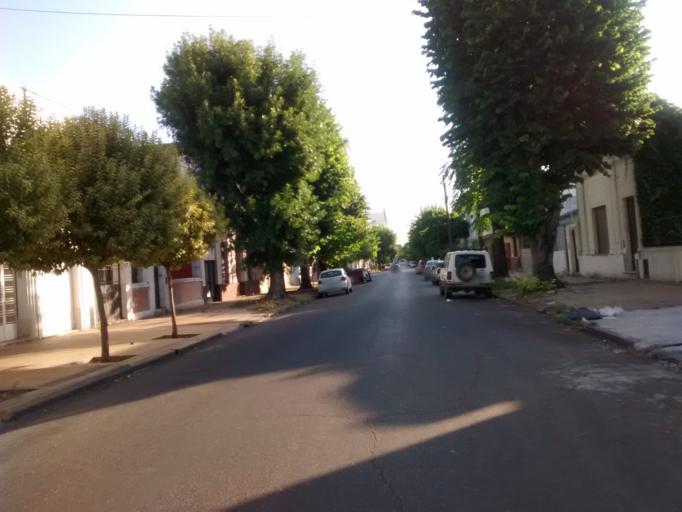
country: AR
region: Buenos Aires
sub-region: Partido de La Plata
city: La Plata
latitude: -34.9197
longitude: -57.9321
